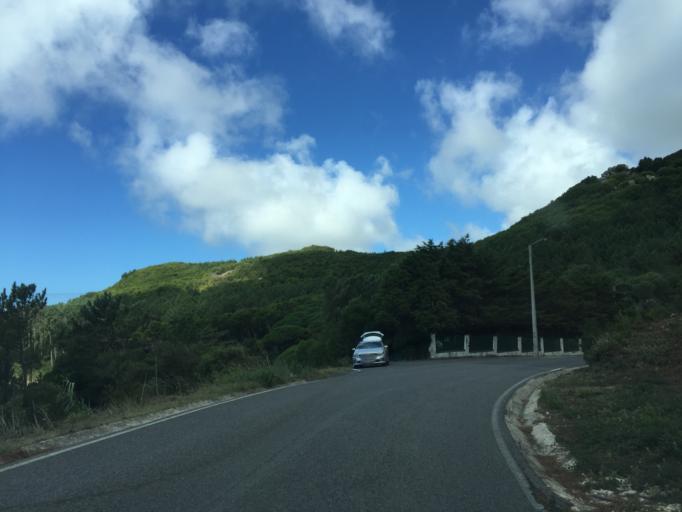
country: PT
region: Lisbon
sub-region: Cascais
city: Alcabideche
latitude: 38.7584
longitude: -9.4361
